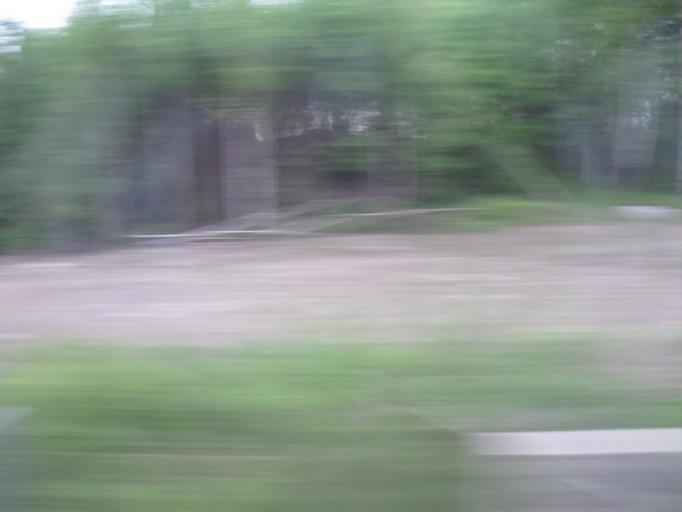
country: NO
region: Oppland
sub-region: Lillehammer
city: Lillehammer
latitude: 61.1378
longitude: 10.4240
